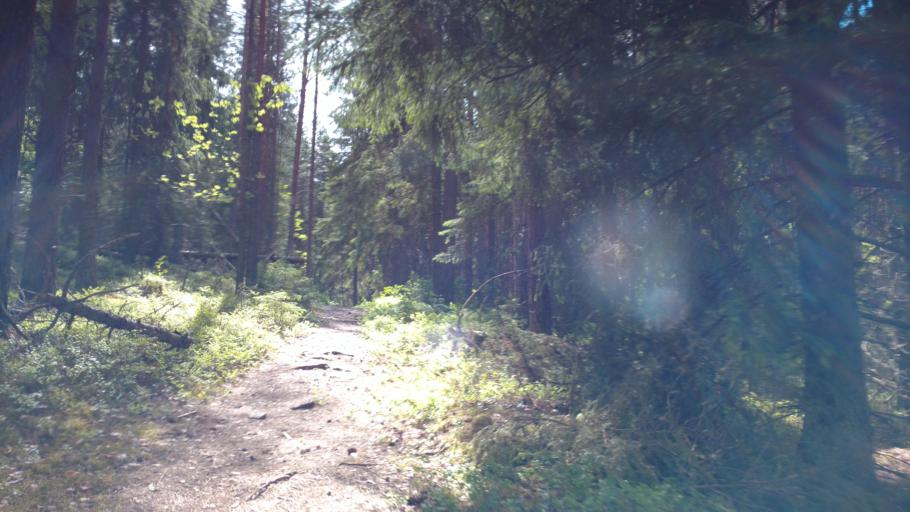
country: FI
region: Varsinais-Suomi
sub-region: Salo
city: Salo
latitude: 60.3676
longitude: 23.1826
